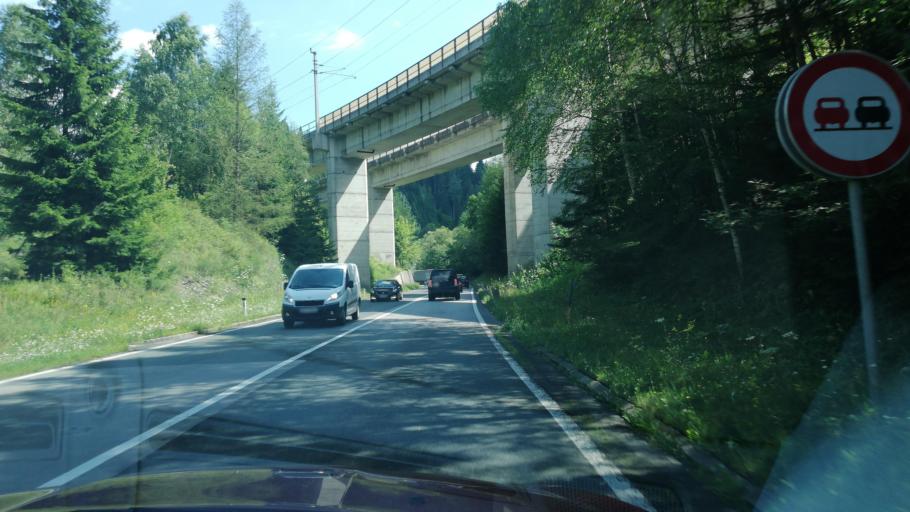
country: AT
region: Styria
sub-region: Politischer Bezirk Murau
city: Sankt Marein bei Neumarkt
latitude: 47.0374
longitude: 14.4245
